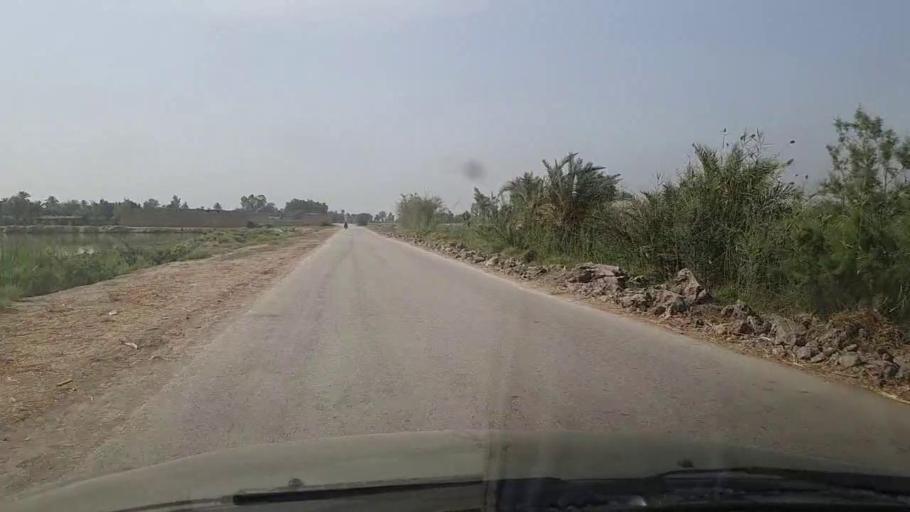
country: PK
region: Sindh
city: Gambat
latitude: 27.4446
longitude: 68.4861
